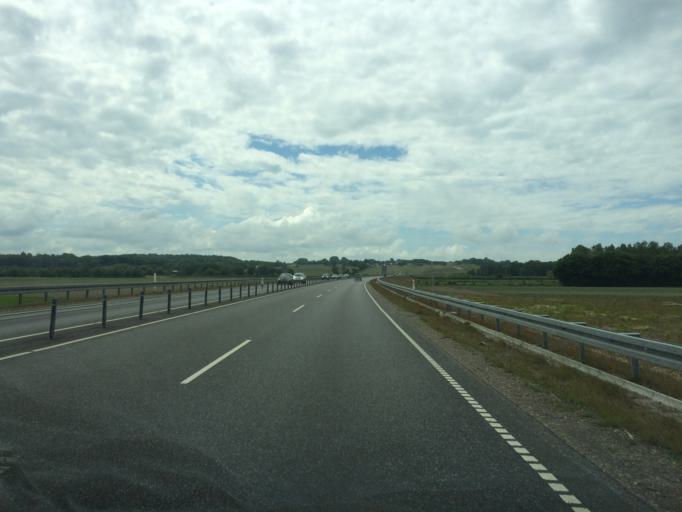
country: DK
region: Zealand
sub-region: Odsherred Kommune
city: Hojby
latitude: 55.8382
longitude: 11.5994
